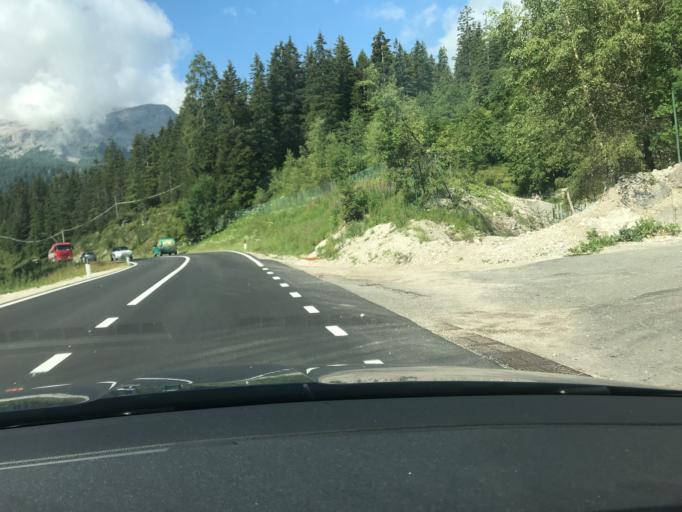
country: IT
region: Trentino-Alto Adige
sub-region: Bolzano
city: Corvara in Badia
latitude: 46.5622
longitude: 11.8837
